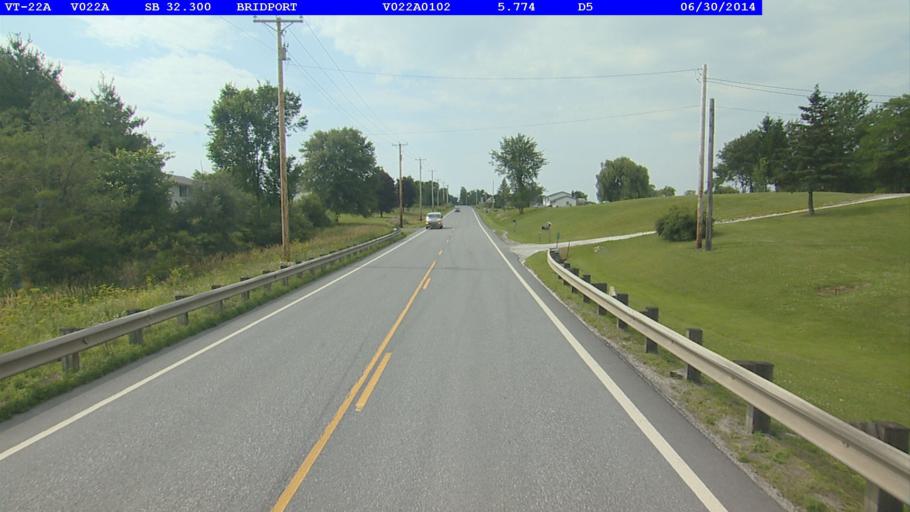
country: US
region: Vermont
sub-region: Addison County
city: Middlebury (village)
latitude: 44.0228
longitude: -73.3112
